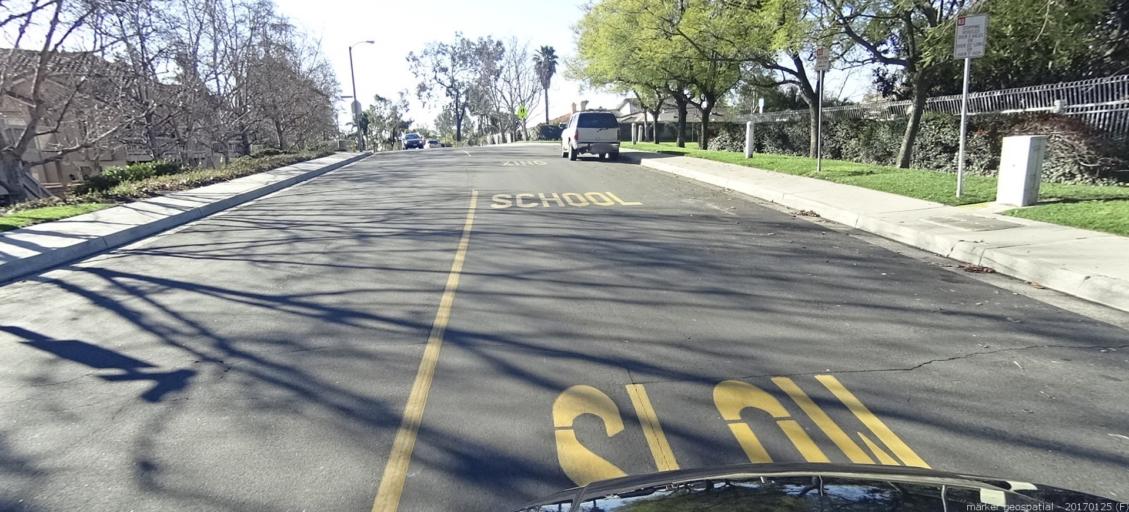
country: US
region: California
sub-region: Orange County
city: Portola Hills
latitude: 33.6873
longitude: -117.6275
